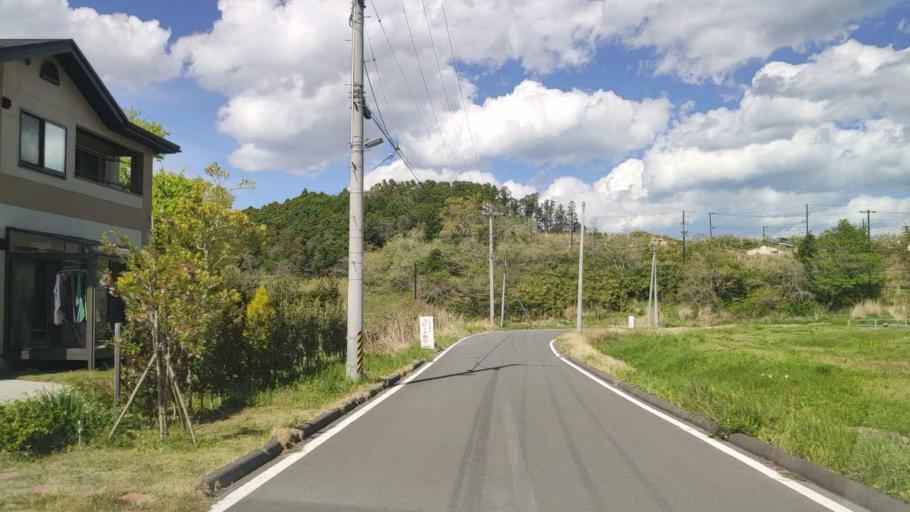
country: JP
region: Miyagi
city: Yamoto
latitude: 38.3362
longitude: 141.1634
